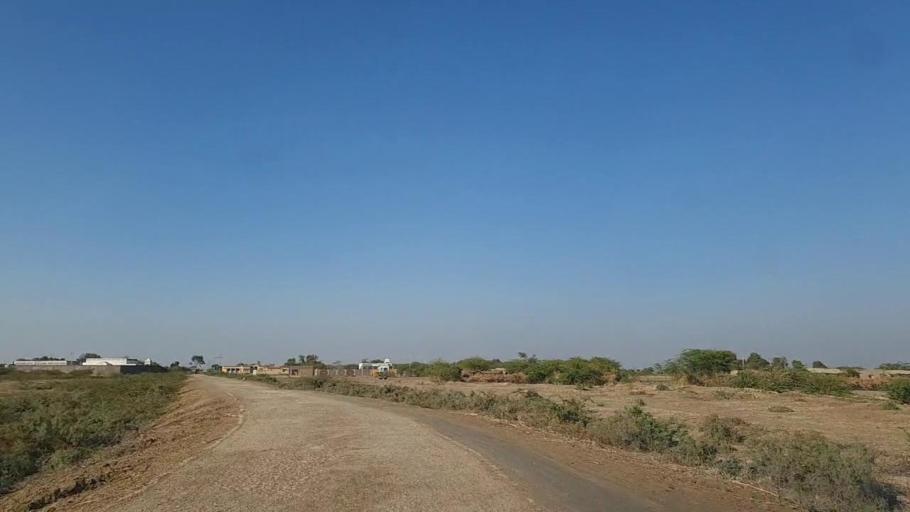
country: PK
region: Sindh
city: Samaro
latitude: 25.3623
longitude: 69.3752
